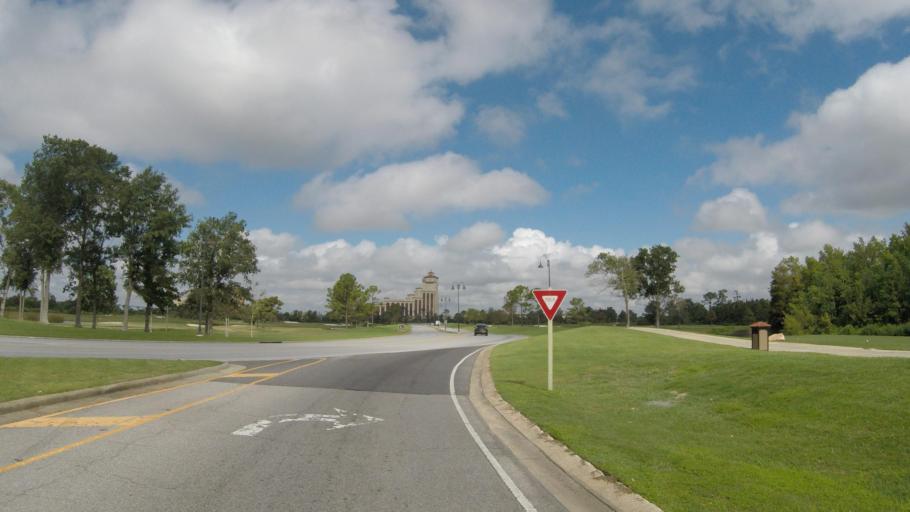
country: US
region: Louisiana
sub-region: Calcasieu Parish
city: Prien
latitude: 30.2022
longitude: -93.2517
